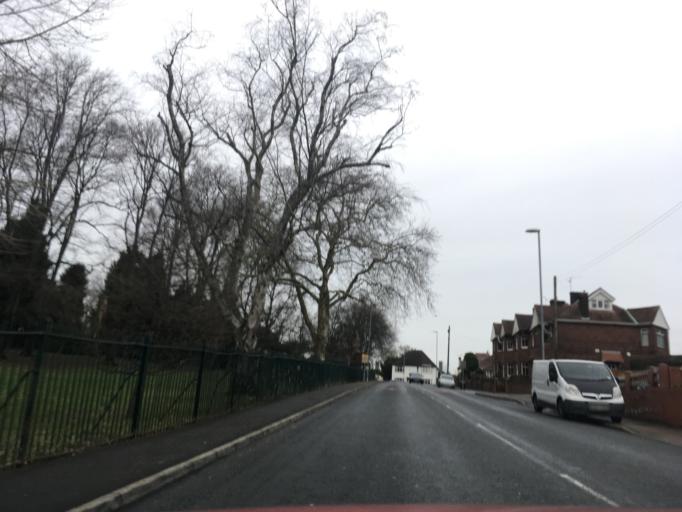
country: GB
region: Wales
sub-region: Newport
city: Caerleon
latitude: 51.5928
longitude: -2.9625
